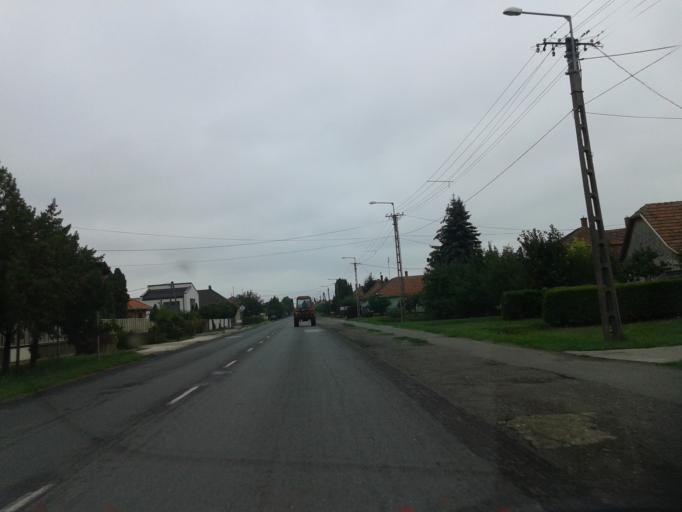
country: HU
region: Bacs-Kiskun
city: Akaszto
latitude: 46.6891
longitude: 19.2065
